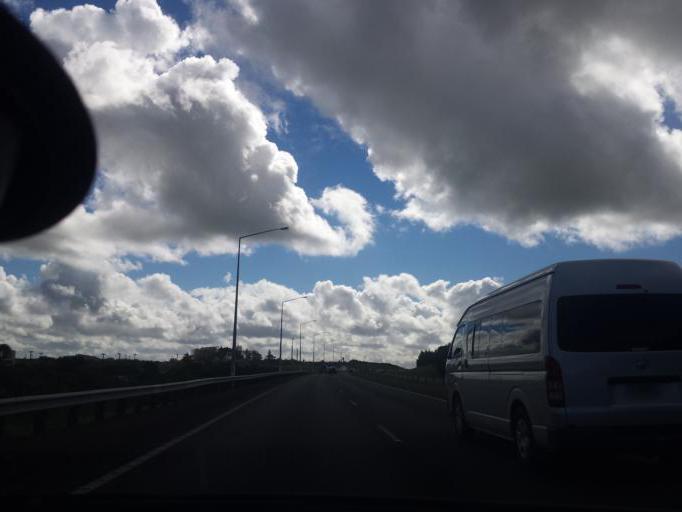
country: NZ
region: Auckland
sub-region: Auckland
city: Rothesay Bay
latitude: -36.6604
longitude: 174.6685
